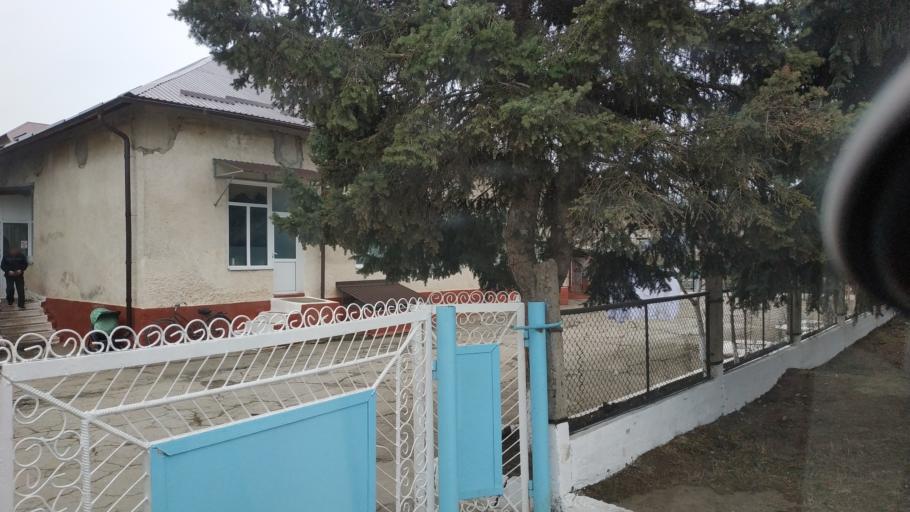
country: MD
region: Telenesti
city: Cocieri
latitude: 47.3793
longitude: 29.1203
